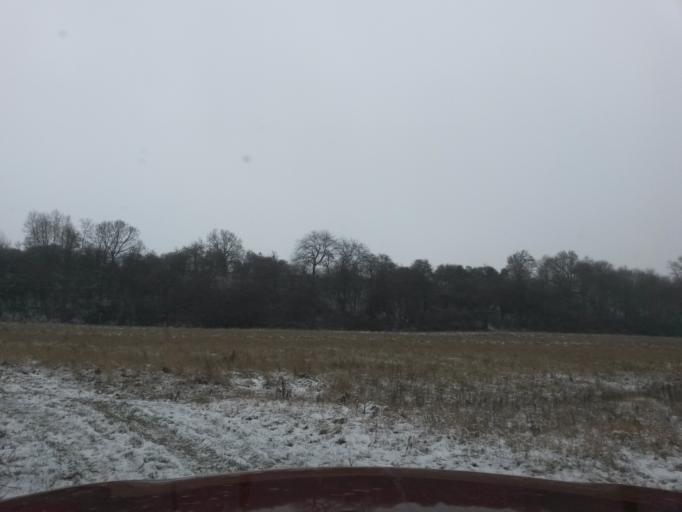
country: SK
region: Presovsky
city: Sabinov
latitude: 48.9986
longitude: 21.1141
